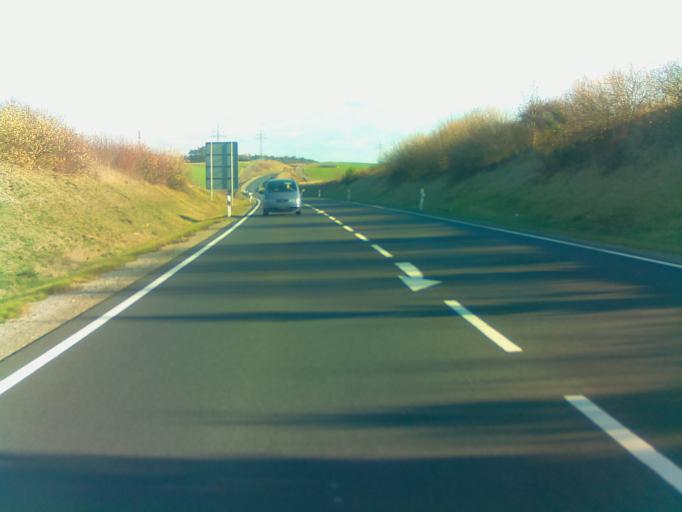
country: DE
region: Bavaria
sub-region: Regierungsbezirk Unterfranken
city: Rodelmaier
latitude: 50.3290
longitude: 10.2744
